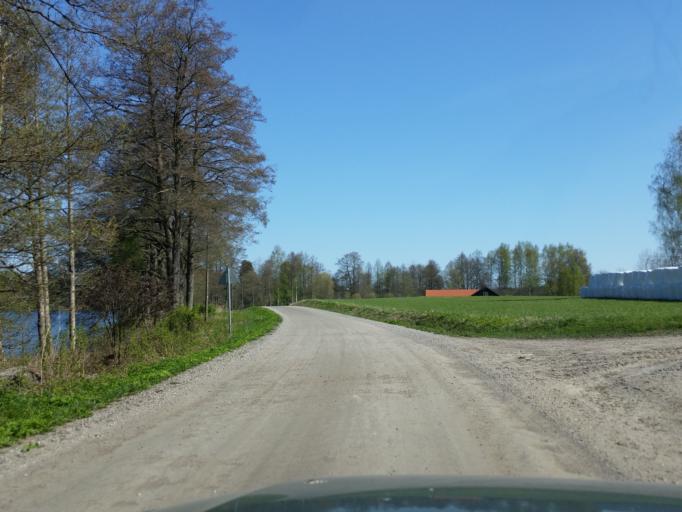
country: FI
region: Uusimaa
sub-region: Helsinki
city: Karjalohja
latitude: 60.1817
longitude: 23.6388
